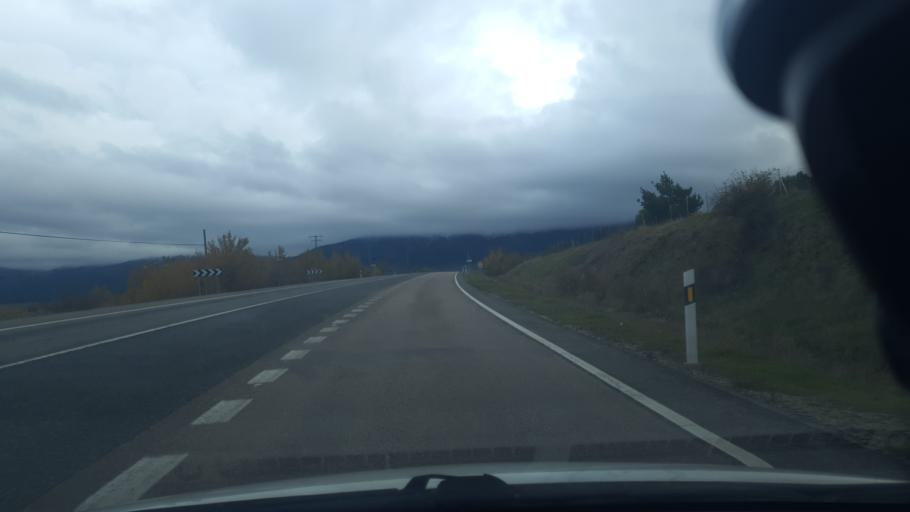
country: ES
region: Castille and Leon
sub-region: Provincia de Segovia
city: Cerezo de Abajo
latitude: 41.2150
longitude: -3.5873
